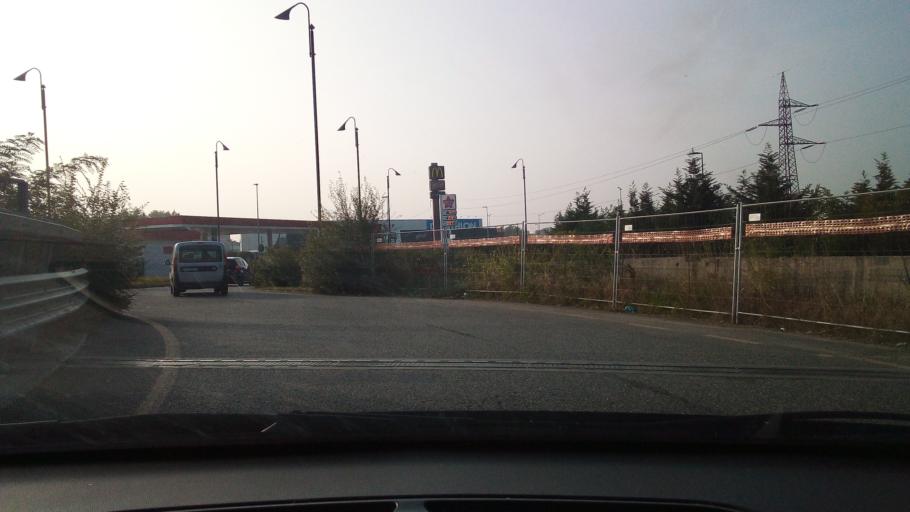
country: IT
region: Lombardy
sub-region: Citta metropolitana di Milano
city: Novegro-Tregarezzo-San Felice
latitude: 45.4875
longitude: 9.2638
